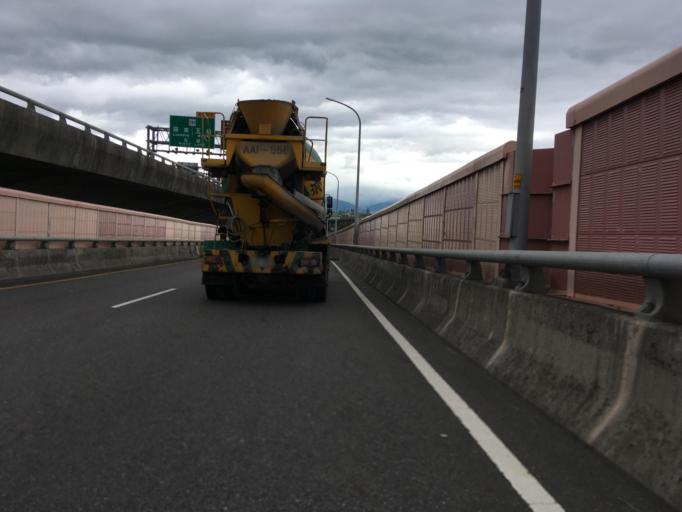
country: TW
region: Taiwan
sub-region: Yilan
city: Yilan
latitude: 24.6619
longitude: 121.8008
